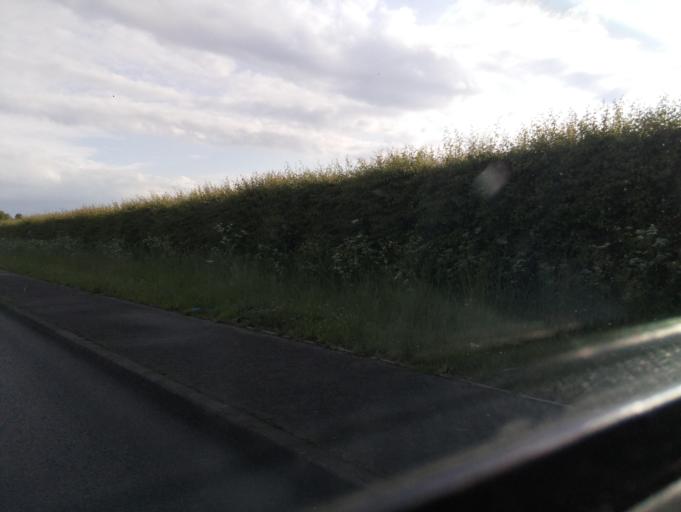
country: GB
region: England
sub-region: Lincolnshire
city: Navenby
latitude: 53.0671
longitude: -0.6358
